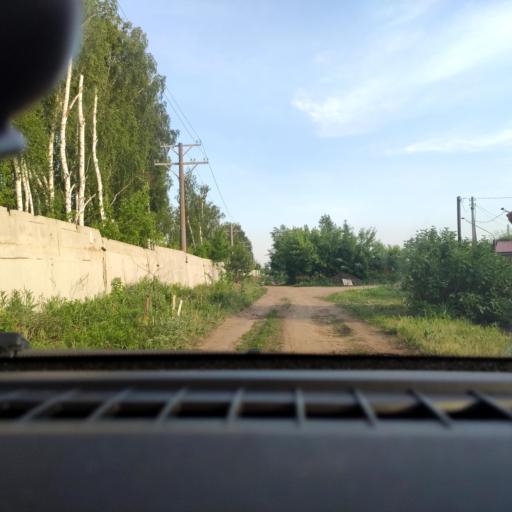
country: RU
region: Samara
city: Tol'yatti
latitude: 53.5967
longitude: 49.3246
